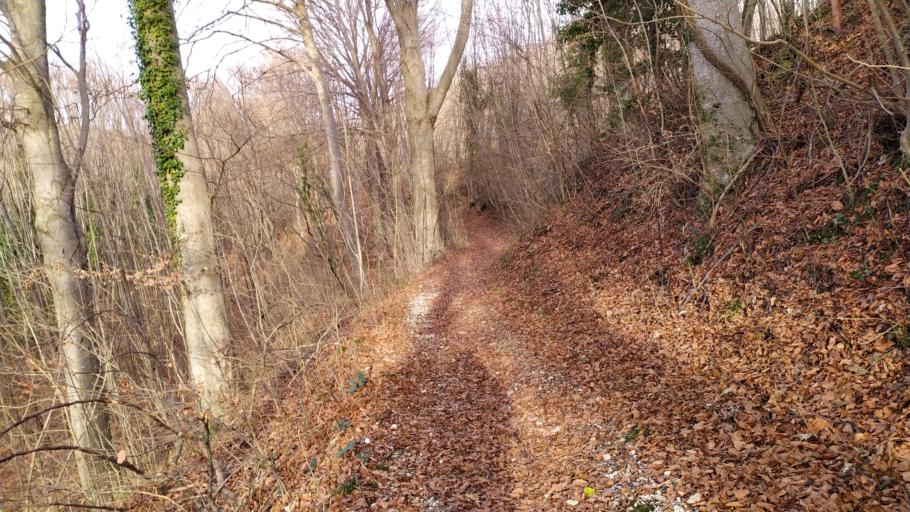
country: IT
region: Veneto
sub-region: Provincia di Vicenza
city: Velo d'Astico
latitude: 45.7609
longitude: 11.3581
